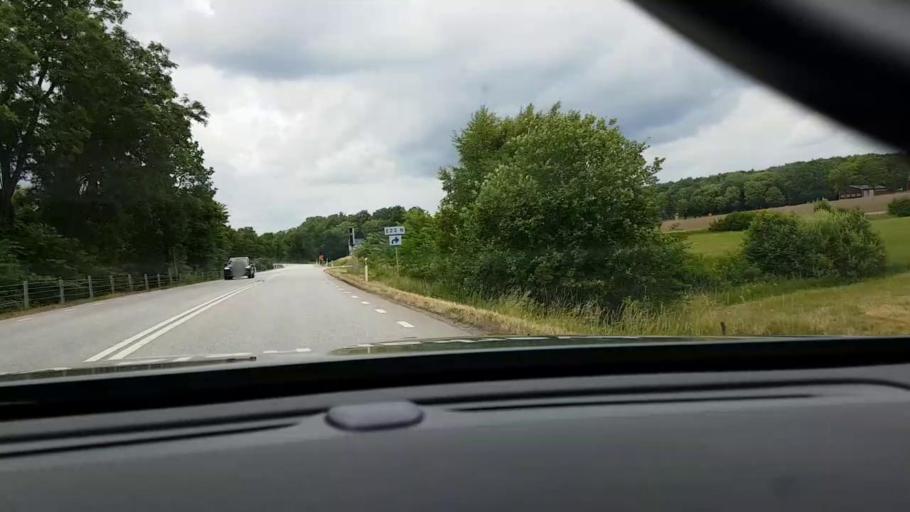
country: SE
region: Skane
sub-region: Horby Kommun
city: Hoerby
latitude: 55.8765
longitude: 13.6319
